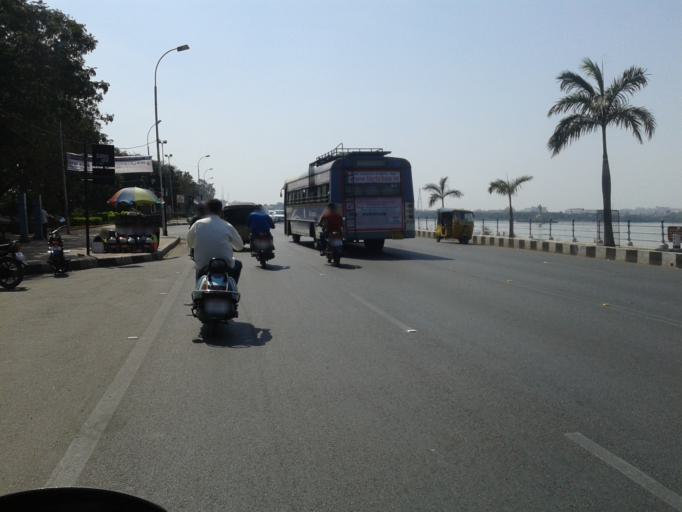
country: IN
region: Telangana
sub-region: Hyderabad
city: Hyderabad
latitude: 17.4188
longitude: 78.4824
